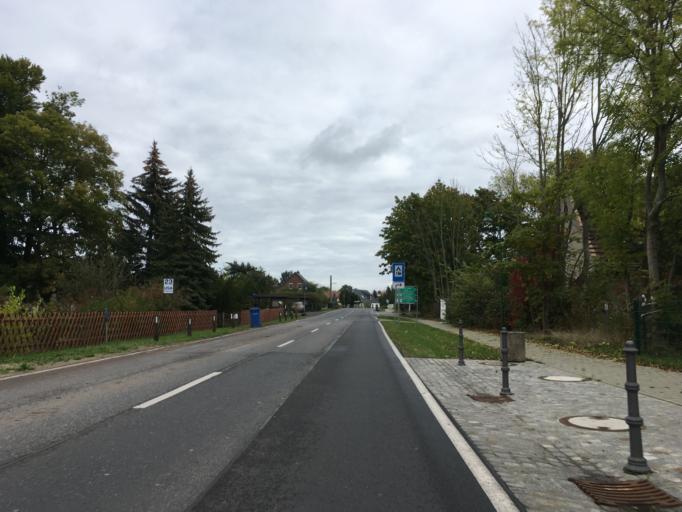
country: DE
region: Brandenburg
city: Werftpfuhl
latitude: 52.6830
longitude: 13.8410
